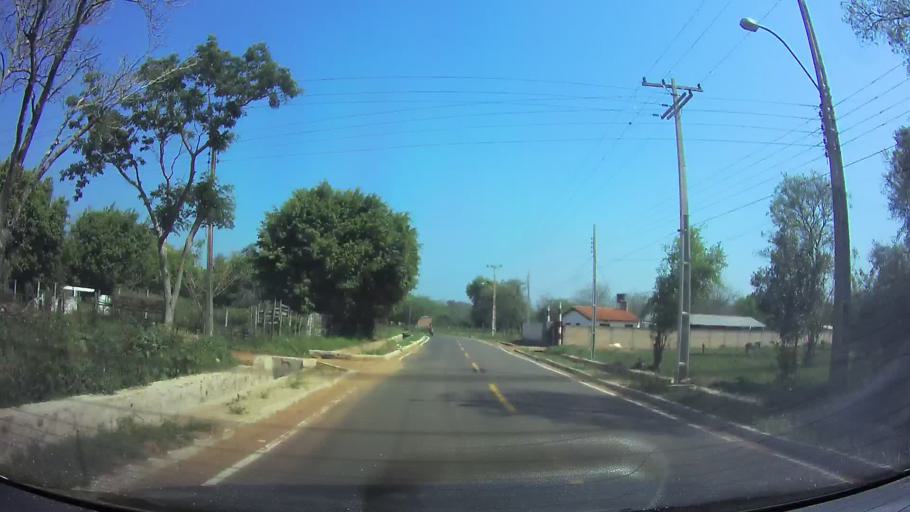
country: PY
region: Central
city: Limpio
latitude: -25.2307
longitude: -57.4906
